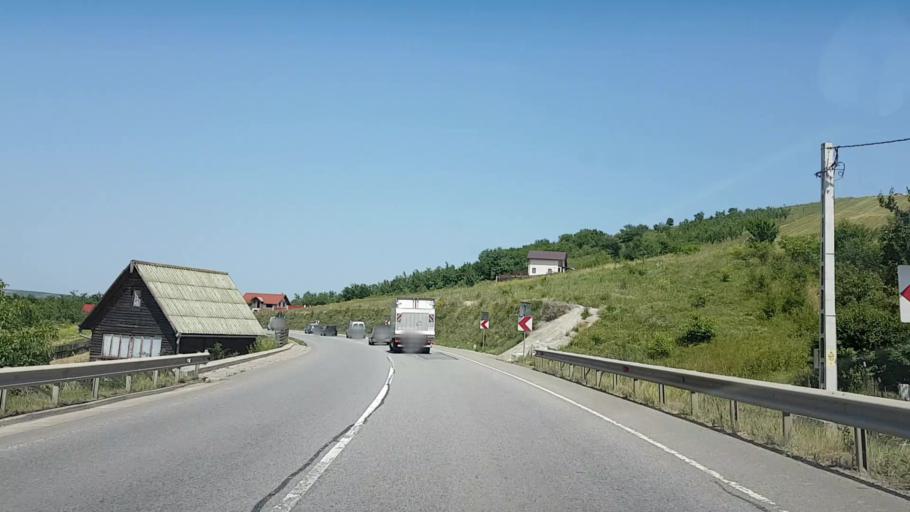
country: RO
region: Cluj
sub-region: Comuna Apahida
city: Dezmir
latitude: 46.7716
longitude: 23.7002
